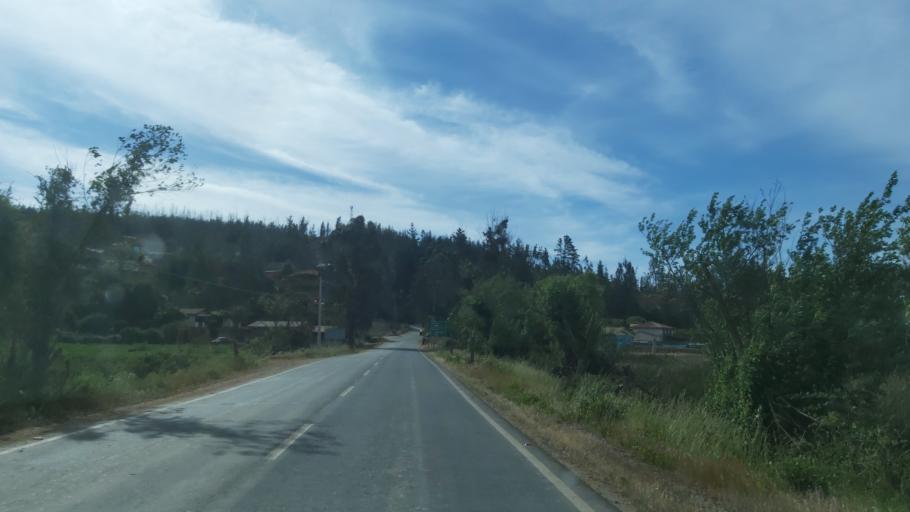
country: CL
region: Maule
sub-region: Provincia de Talca
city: Constitucion
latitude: -34.8498
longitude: -72.0444
